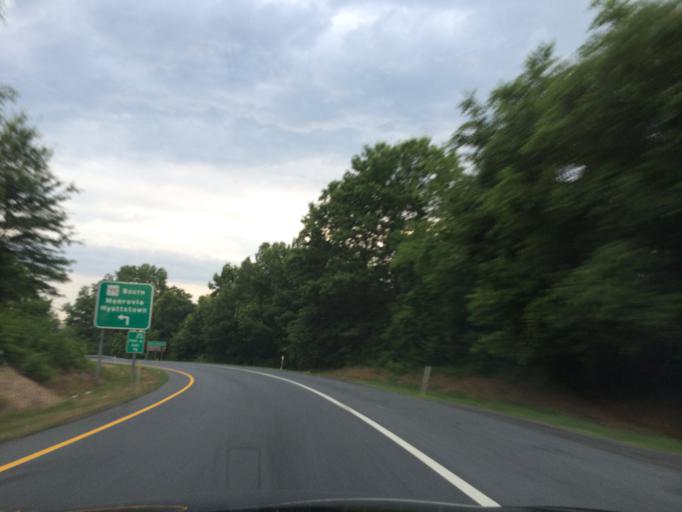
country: US
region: Maryland
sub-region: Frederick County
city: Linganore
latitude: 39.3825
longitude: -77.2578
